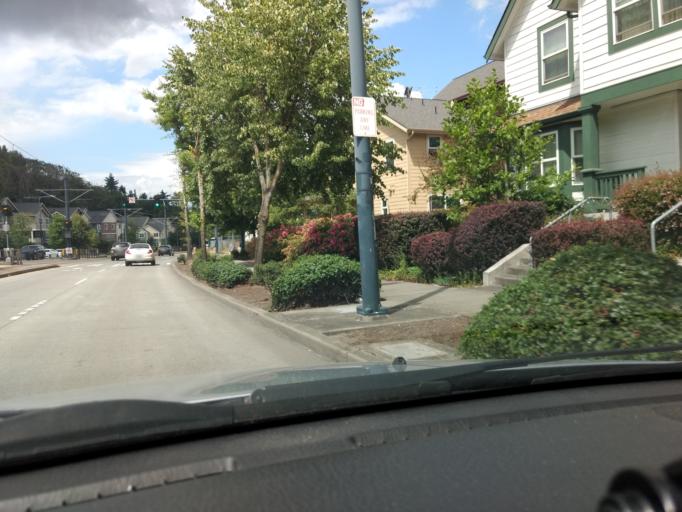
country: US
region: Washington
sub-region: King County
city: Seattle
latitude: 47.5659
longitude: -122.2965
